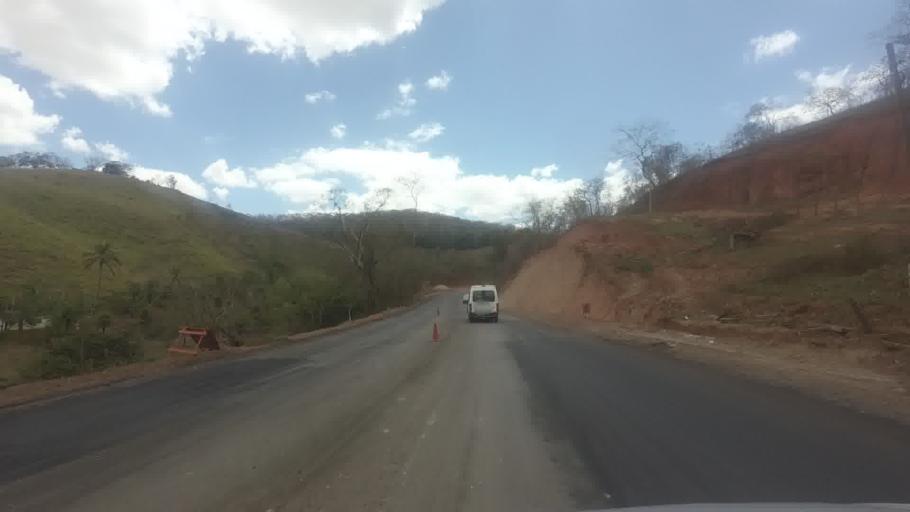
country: BR
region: Rio de Janeiro
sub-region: Santo Antonio De Padua
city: Santo Antonio de Padua
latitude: -21.5090
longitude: -42.0876
